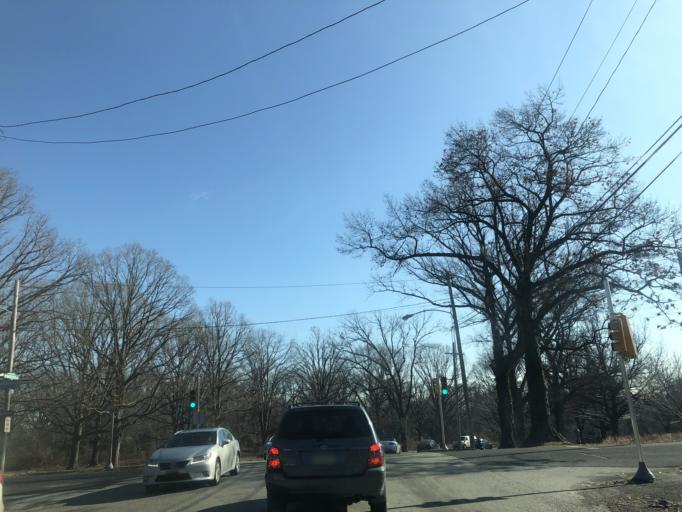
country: US
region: Pennsylvania
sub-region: Montgomery County
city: Bala-Cynwyd
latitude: 39.9901
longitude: -75.2197
